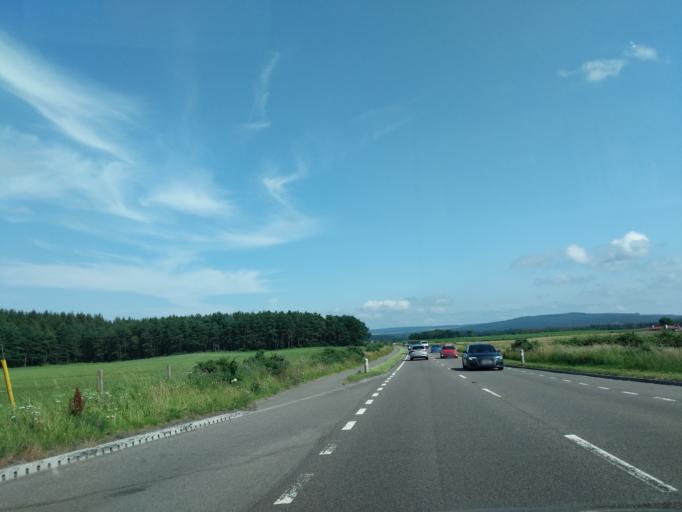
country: GB
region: Scotland
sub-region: Moray
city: Fochabers
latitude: 57.6268
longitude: -3.1570
